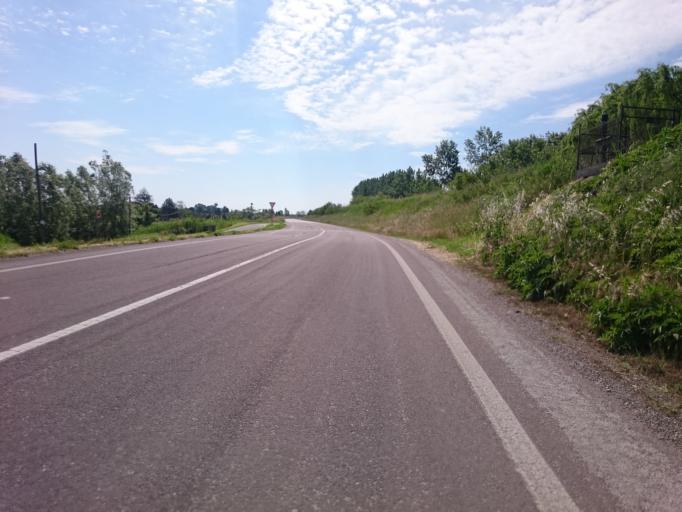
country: IT
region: Veneto
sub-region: Provincia di Rovigo
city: Ariano
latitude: 44.9590
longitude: 12.1159
